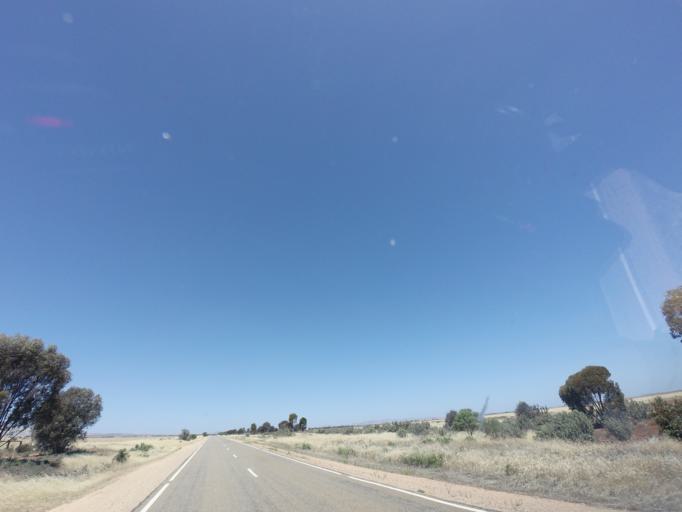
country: AU
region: South Australia
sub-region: Flinders Ranges
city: Quorn
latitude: -32.6822
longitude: 138.3072
